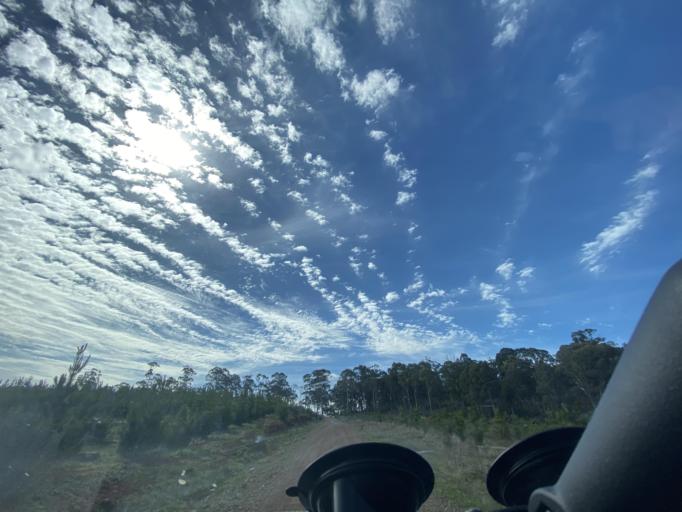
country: AU
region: Victoria
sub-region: Mansfield
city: Mansfield
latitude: -36.8189
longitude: 146.1022
